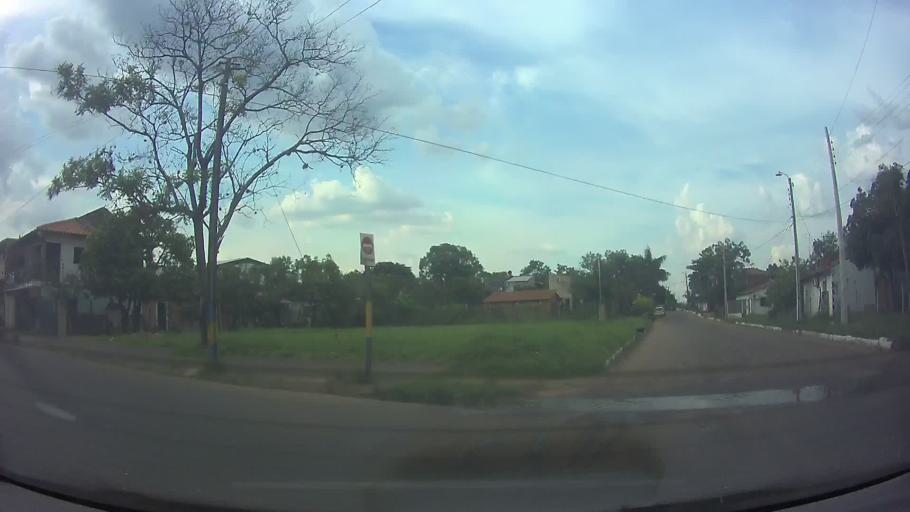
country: PY
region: Central
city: San Lorenzo
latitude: -25.2685
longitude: -57.4775
